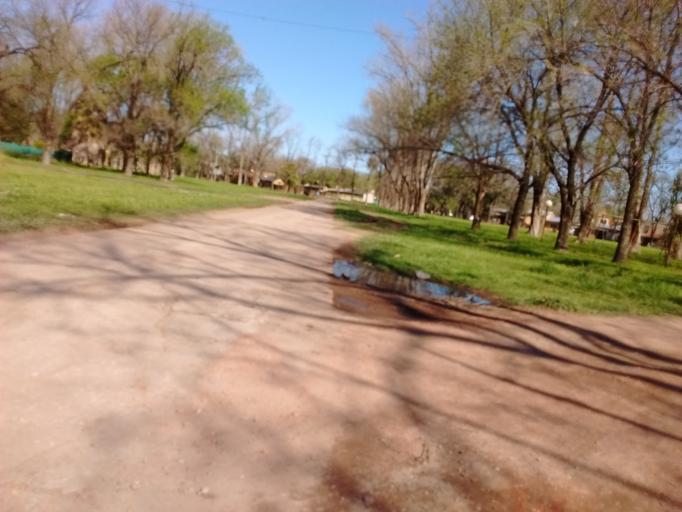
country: AR
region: Santa Fe
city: Funes
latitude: -32.9178
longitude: -60.8528
